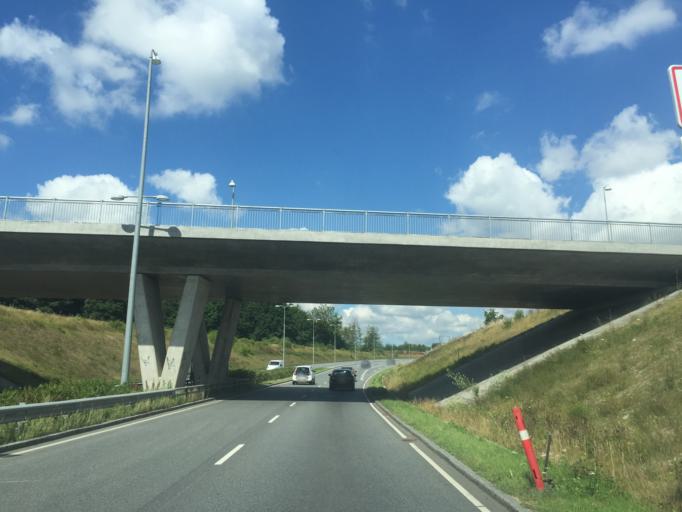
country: DK
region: South Denmark
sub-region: Odense Kommune
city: Stige
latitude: 55.4229
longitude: 10.4110
